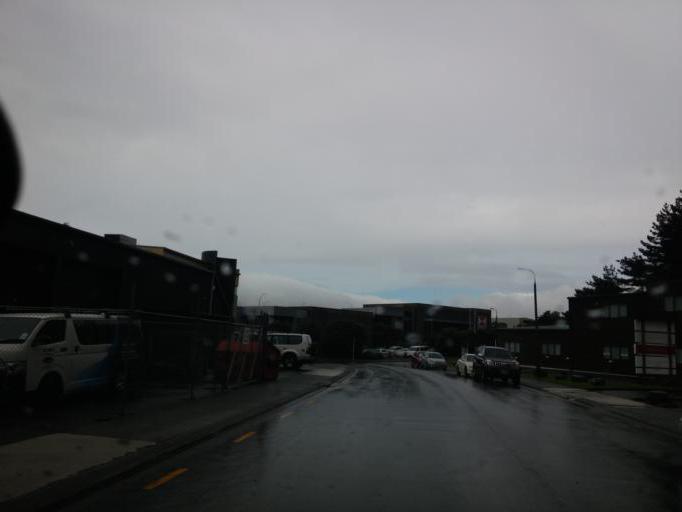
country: NZ
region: Wellington
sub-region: Wellington City
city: Wellington
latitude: -41.2464
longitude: 174.8124
